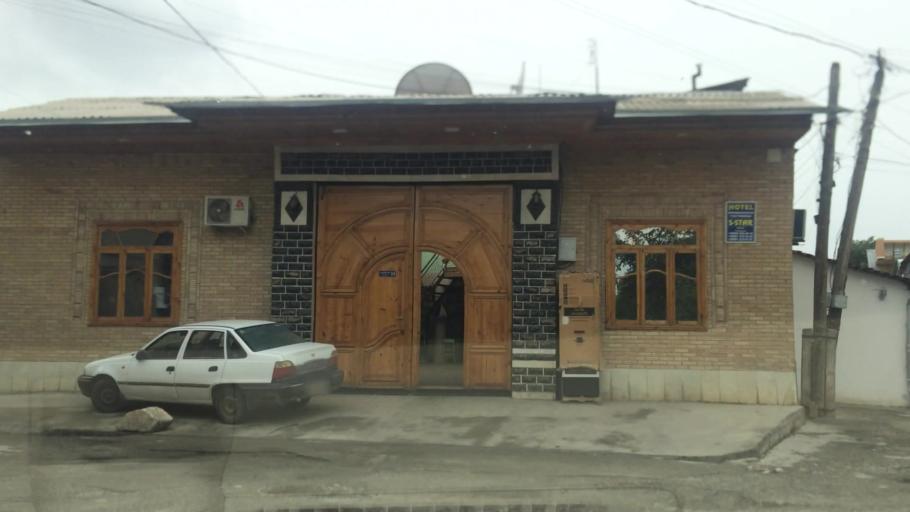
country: UZ
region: Samarqand
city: Samarqand
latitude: 39.6523
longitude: 66.9762
